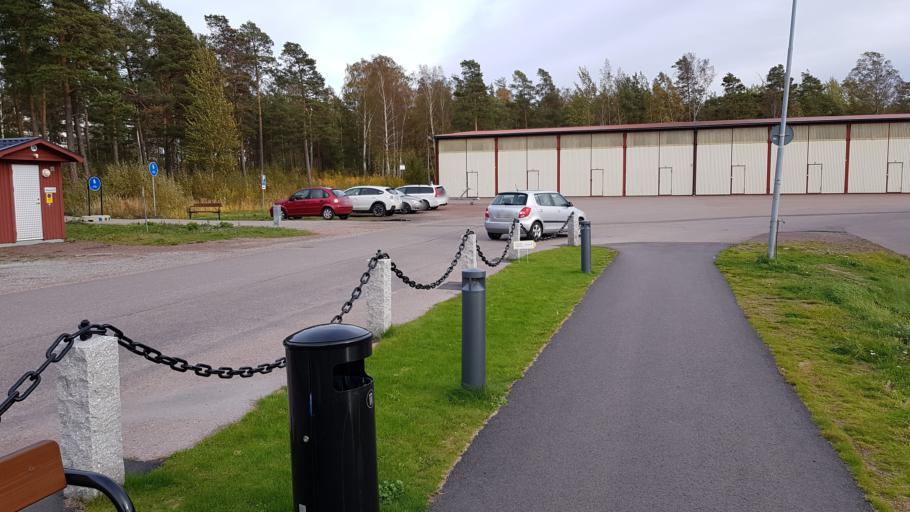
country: SE
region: Vaermland
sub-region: Hammaro Kommun
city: Skoghall
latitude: 59.3170
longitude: 13.4668
